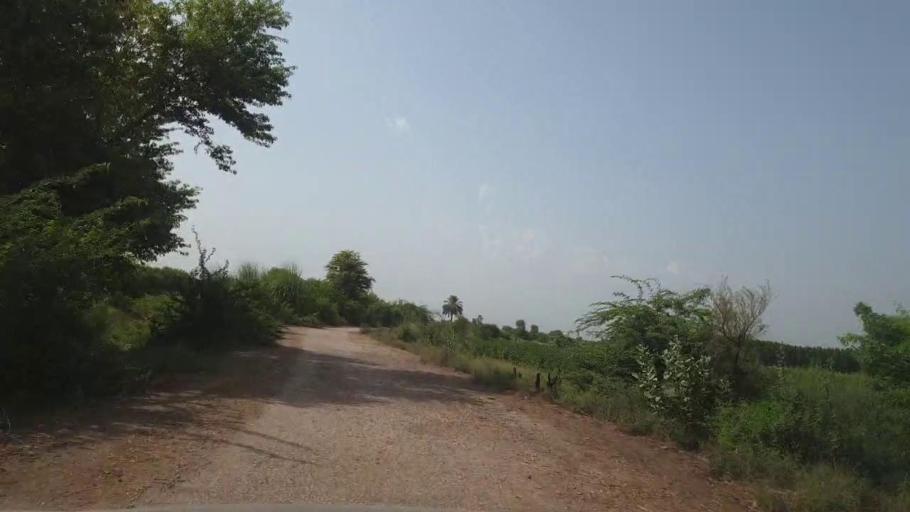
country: PK
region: Sindh
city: Pano Aqil
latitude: 27.7786
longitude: 69.1607
